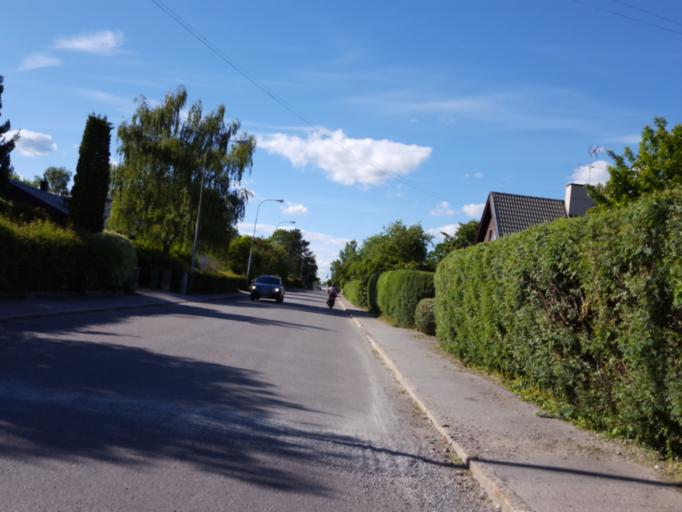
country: SE
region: Stockholm
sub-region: Sollentuna Kommun
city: Sollentuna
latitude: 59.4329
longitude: 17.9392
